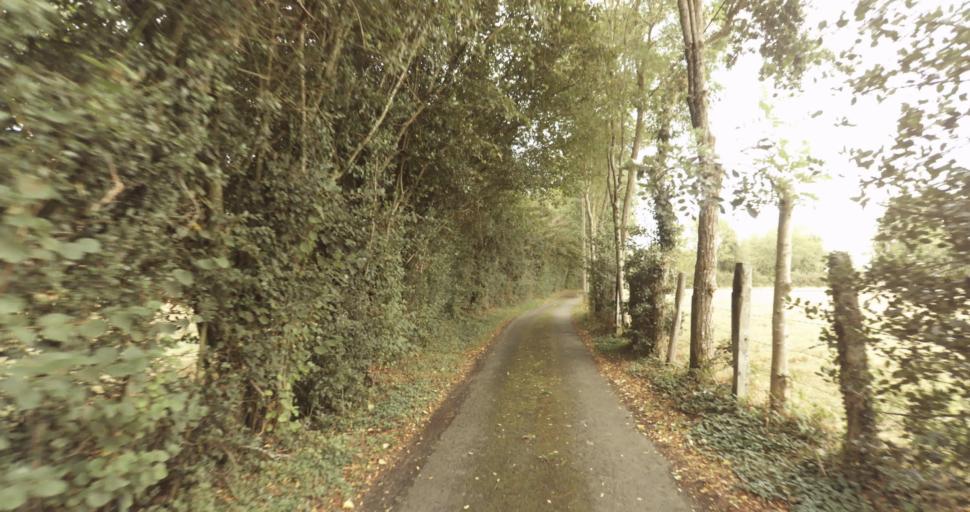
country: FR
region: Lower Normandy
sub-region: Departement de l'Orne
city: Gace
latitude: 48.8590
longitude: 0.3194
